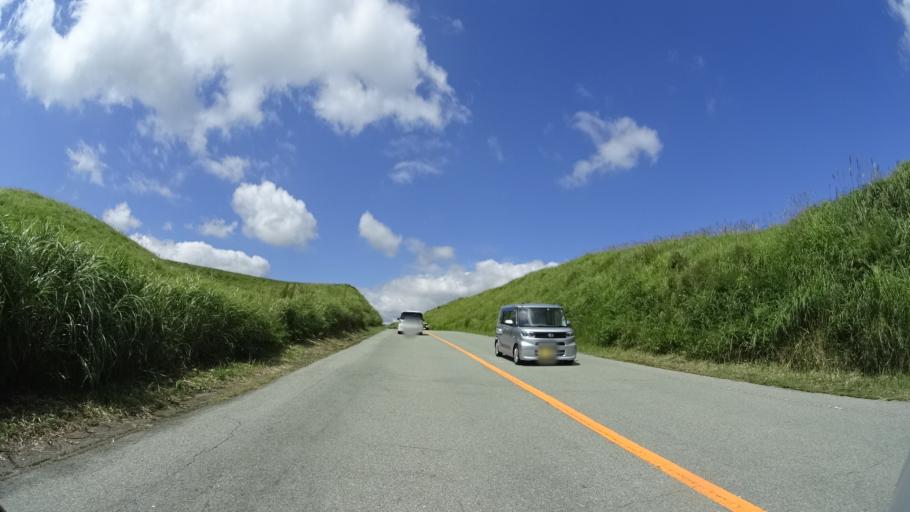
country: JP
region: Kumamoto
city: Aso
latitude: 33.0060
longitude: 131.1253
